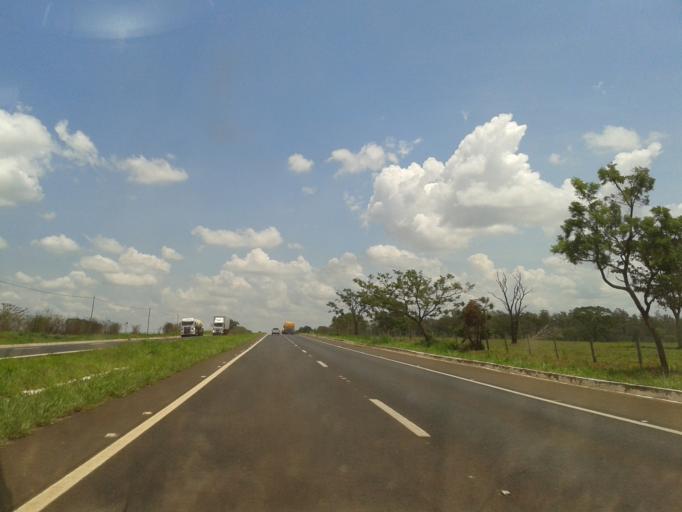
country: BR
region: Minas Gerais
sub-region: Uberlandia
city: Uberlandia
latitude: -18.8781
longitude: -48.5092
